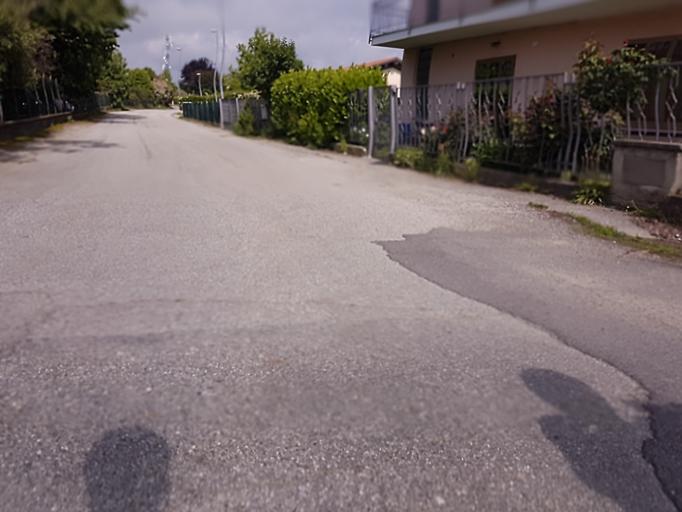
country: IT
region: Piedmont
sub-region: Provincia di Torino
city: Vialfre
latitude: 45.3823
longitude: 7.8199
